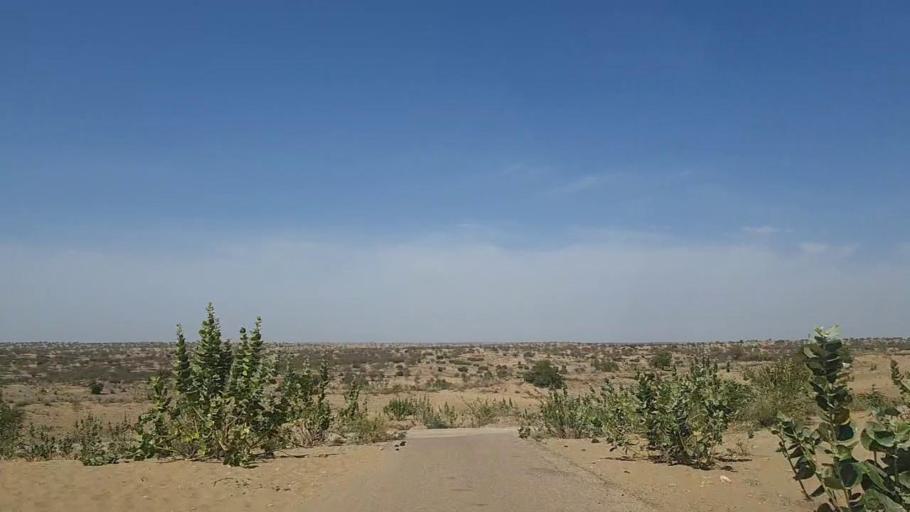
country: PK
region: Sindh
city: Mithi
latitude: 24.8593
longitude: 69.6693
